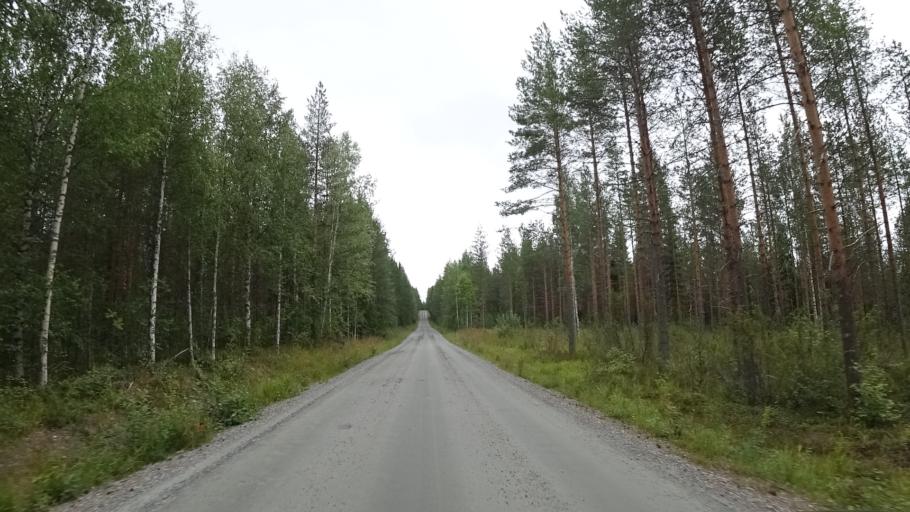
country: FI
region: North Karelia
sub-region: Pielisen Karjala
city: Lieksa
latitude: 63.3767
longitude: 30.3558
